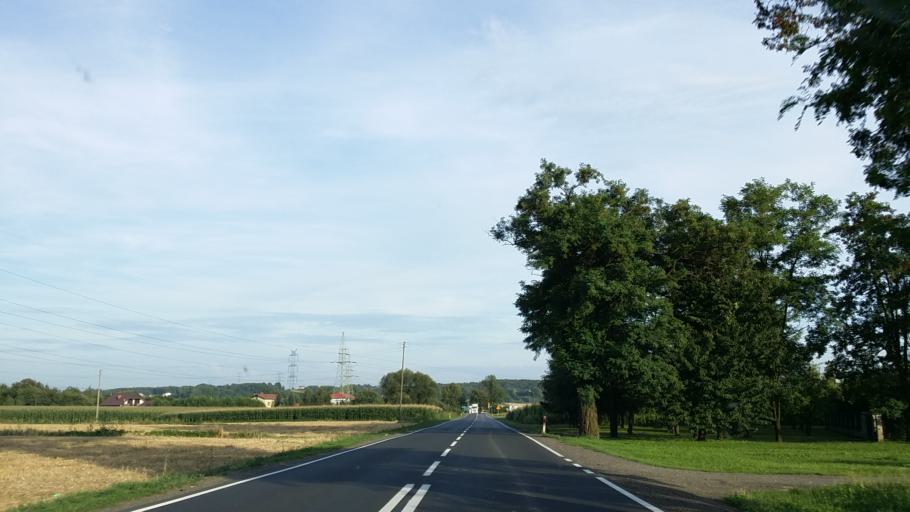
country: PL
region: Lesser Poland Voivodeship
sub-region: Powiat oswiecimski
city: Zator
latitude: 49.9976
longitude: 19.4542
